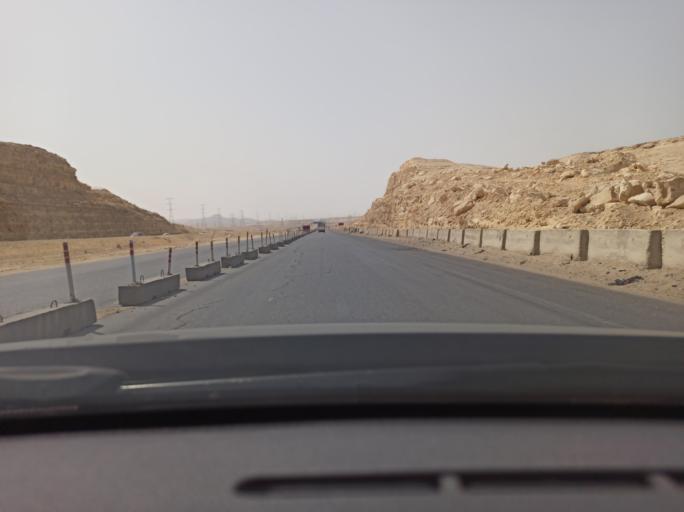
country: EG
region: Muhafazat Bani Suwayf
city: Bush
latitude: 29.1739
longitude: 31.2430
